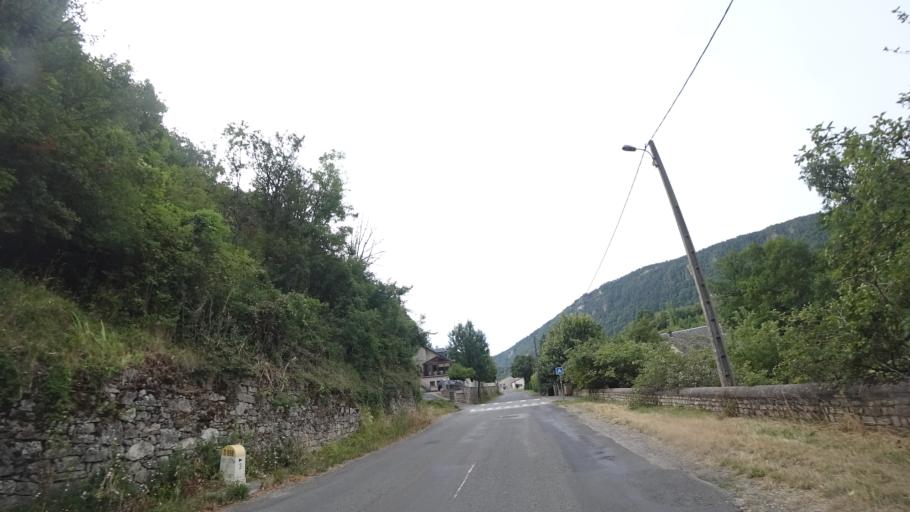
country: FR
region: Languedoc-Roussillon
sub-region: Departement de la Lozere
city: La Canourgue
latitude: 44.4256
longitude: 3.2232
